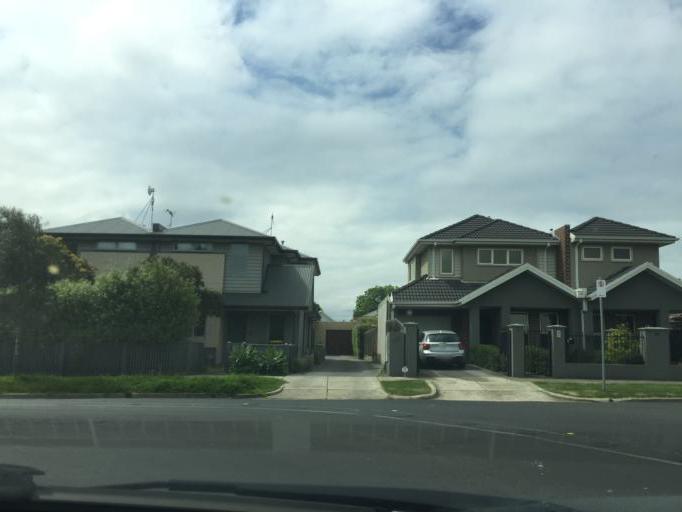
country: AU
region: Victoria
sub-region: Hobsons Bay
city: South Kingsville
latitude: -37.8294
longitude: 144.8747
